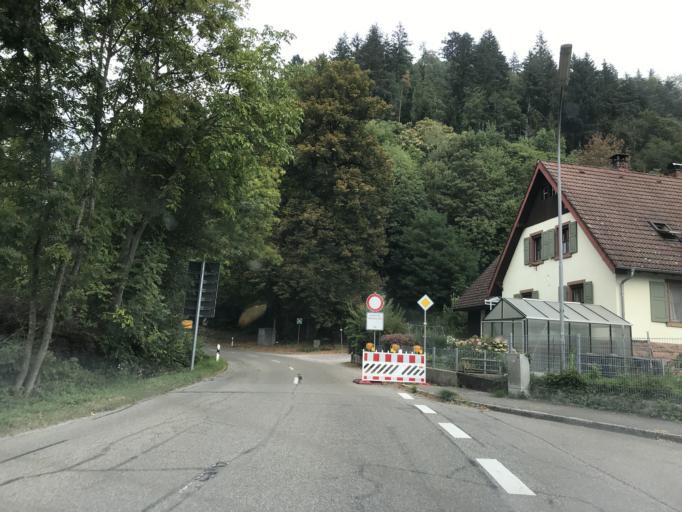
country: DE
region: Baden-Wuerttemberg
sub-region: Freiburg Region
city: Wehr
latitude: 47.6376
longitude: 7.9133
